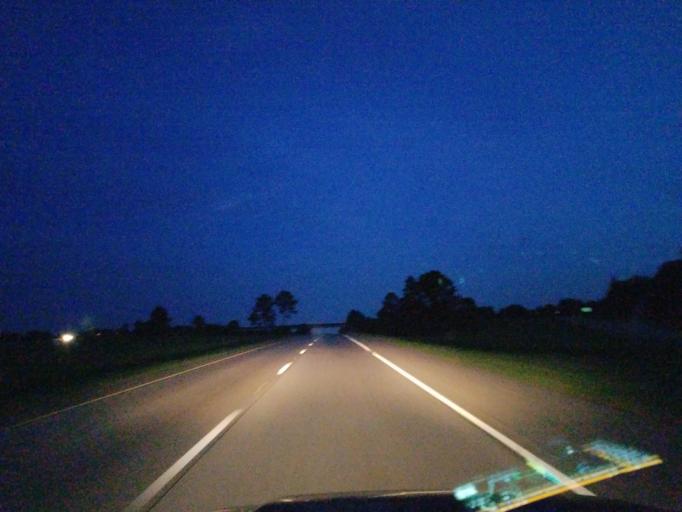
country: US
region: Mississippi
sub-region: Forrest County
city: Rawls Springs
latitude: 31.4720
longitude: -89.3234
